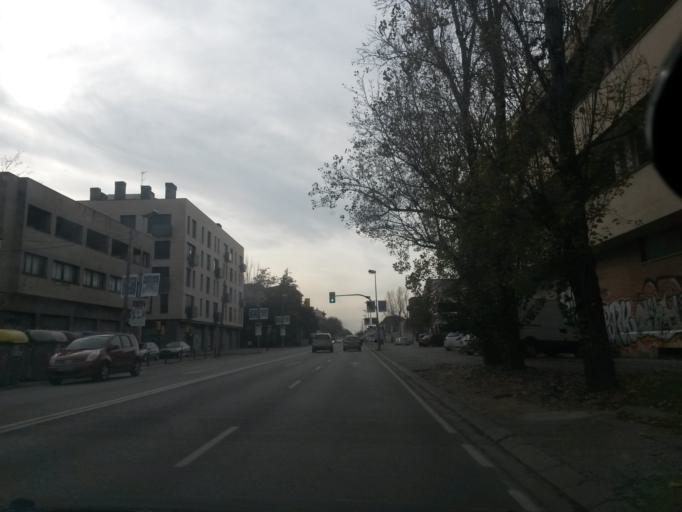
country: ES
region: Catalonia
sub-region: Provincia de Girona
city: Girona
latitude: 41.9682
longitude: 2.8136
